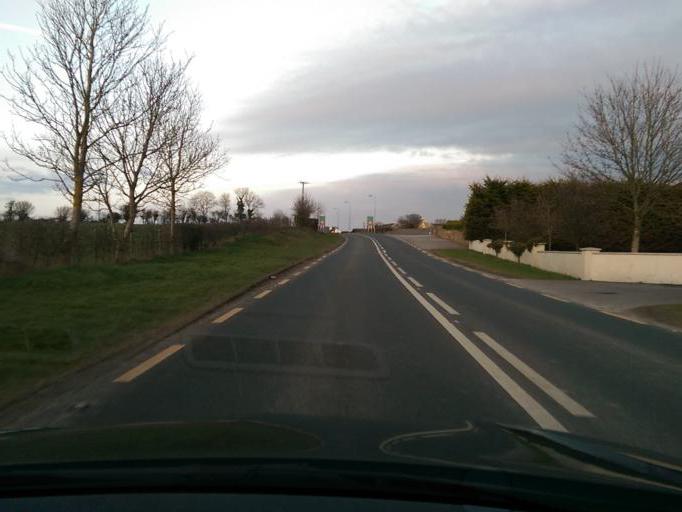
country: IE
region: Munster
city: Nenagh Bridge
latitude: 52.9309
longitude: -8.1626
